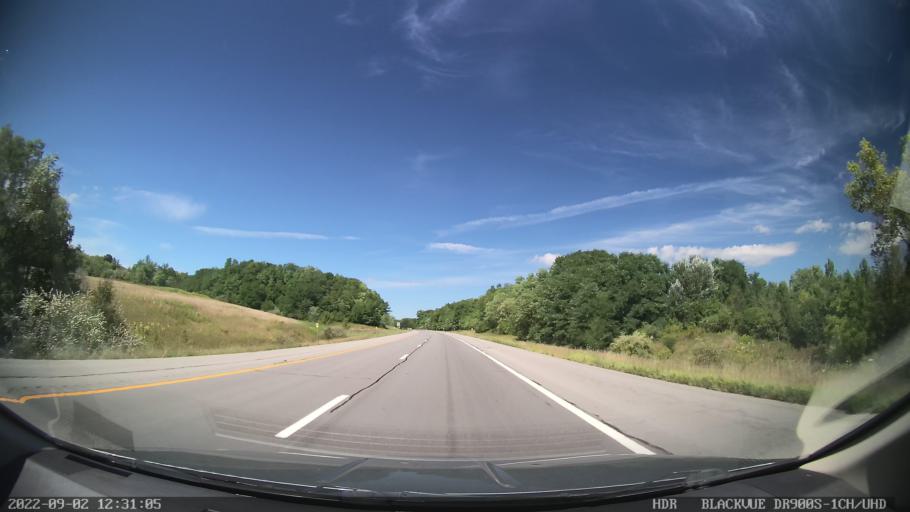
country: US
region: New York
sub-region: Livingston County
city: Dansville
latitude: 42.6036
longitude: -77.7543
